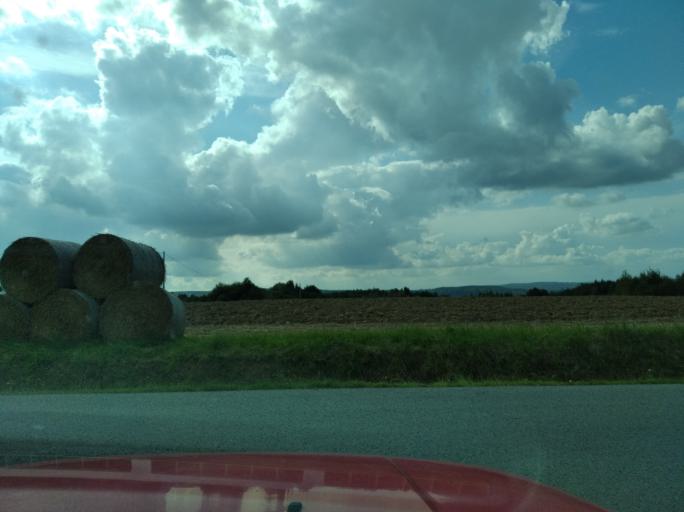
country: PL
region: Subcarpathian Voivodeship
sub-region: Powiat rzeszowski
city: Lubenia
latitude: 49.9387
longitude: 21.9398
